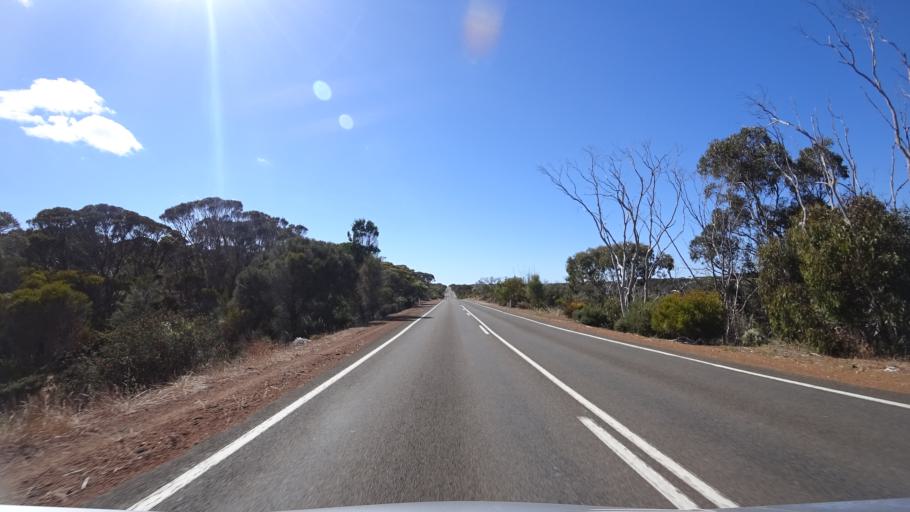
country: AU
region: South Australia
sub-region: Kangaroo Island
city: Kingscote
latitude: -35.7660
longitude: 137.6168
